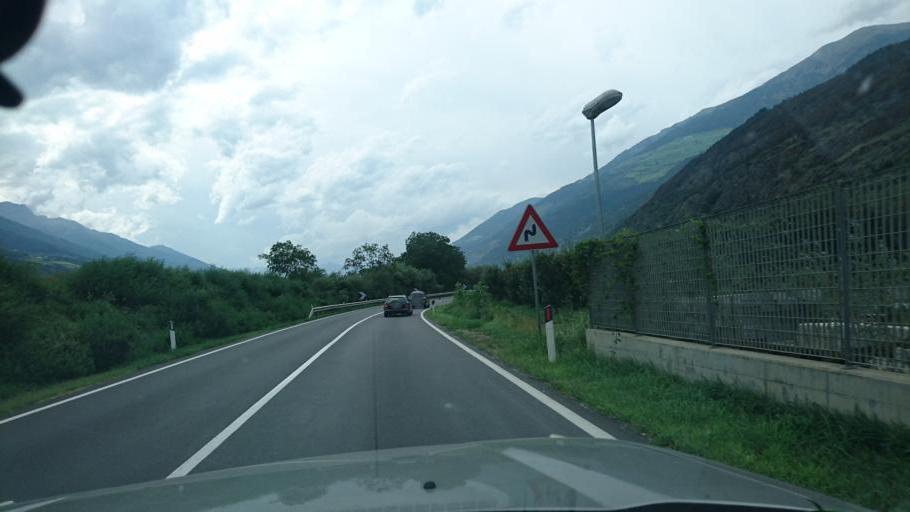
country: IT
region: Trentino-Alto Adige
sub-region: Bolzano
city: Silandro
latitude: 46.6232
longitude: 10.8022
